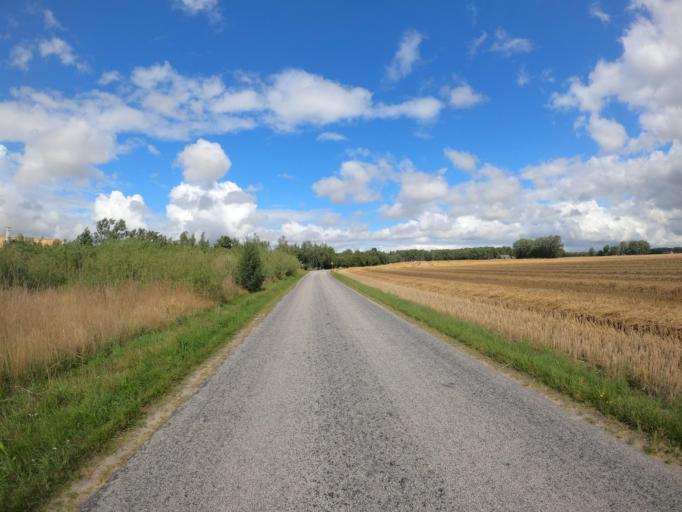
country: SE
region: Skane
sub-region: Eslovs Kommun
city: Eslov
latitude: 55.7298
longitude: 13.3582
